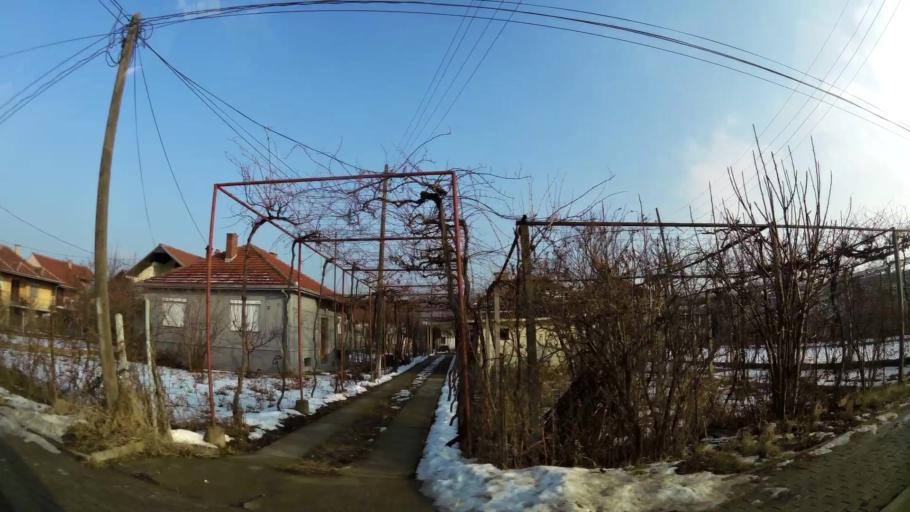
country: MK
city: Miladinovci
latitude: 41.9850
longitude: 21.6511
